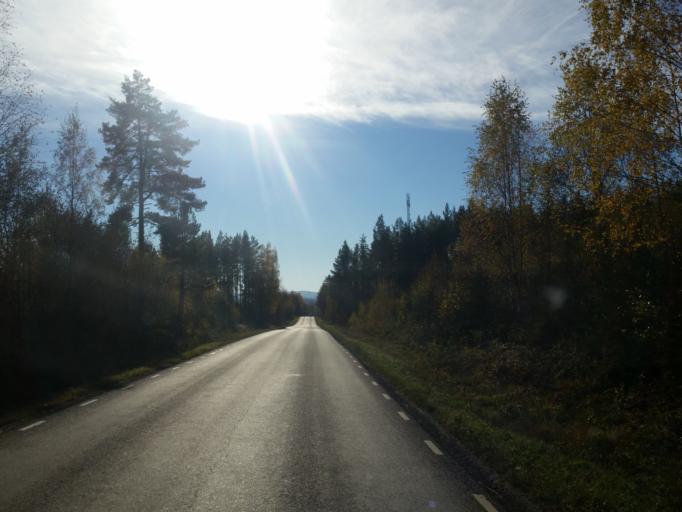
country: SE
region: Dalarna
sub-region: Borlange Kommun
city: Ornas
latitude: 60.5131
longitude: 15.5235
